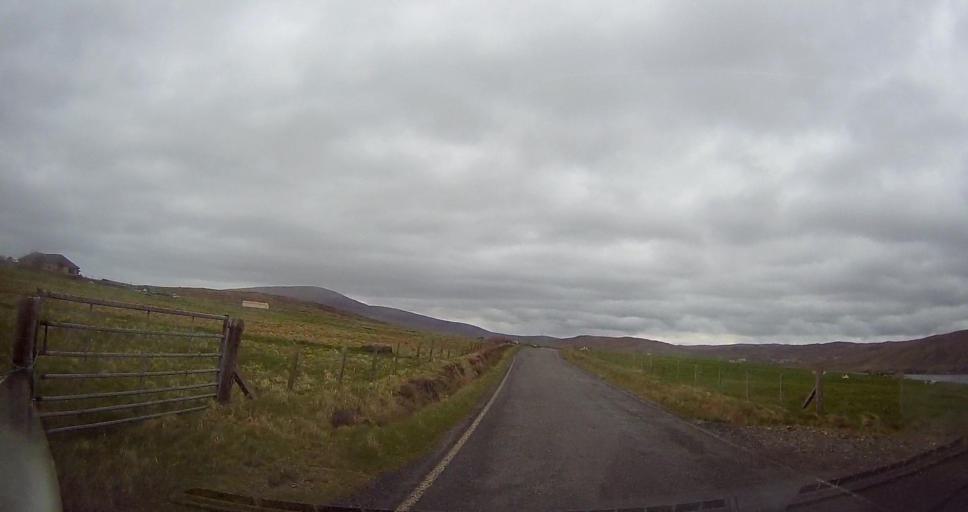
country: GB
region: Scotland
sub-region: Shetland Islands
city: Lerwick
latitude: 60.4802
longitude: -1.4785
